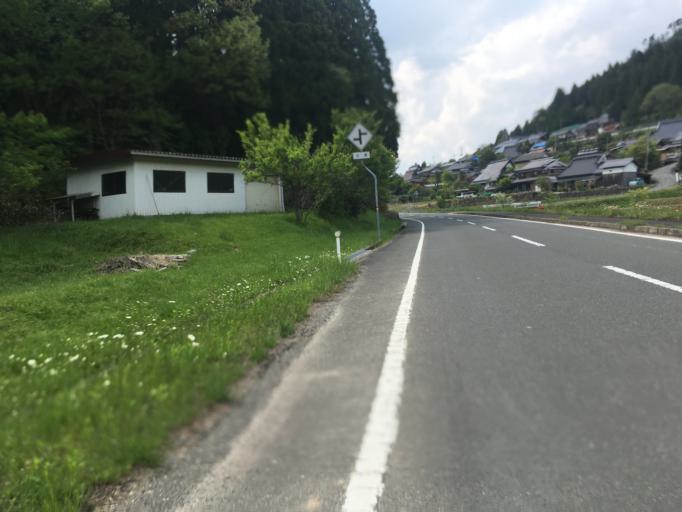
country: JP
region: Kyoto
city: Kameoka
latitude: 35.1079
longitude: 135.5807
